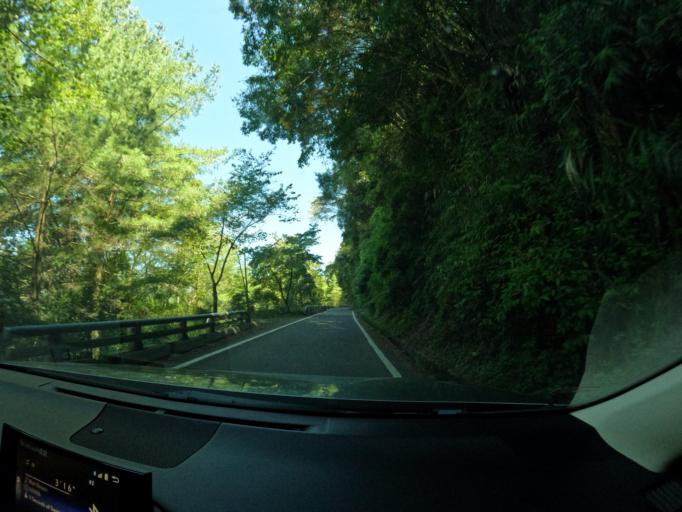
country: TW
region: Taiwan
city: Yujing
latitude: 23.2832
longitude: 120.8773
